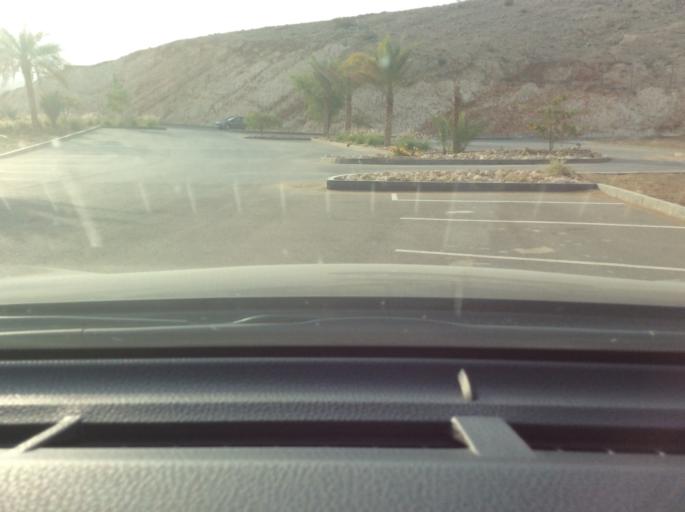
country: OM
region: Muhafazat Masqat
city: Bawshar
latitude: 23.5608
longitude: 58.3889
